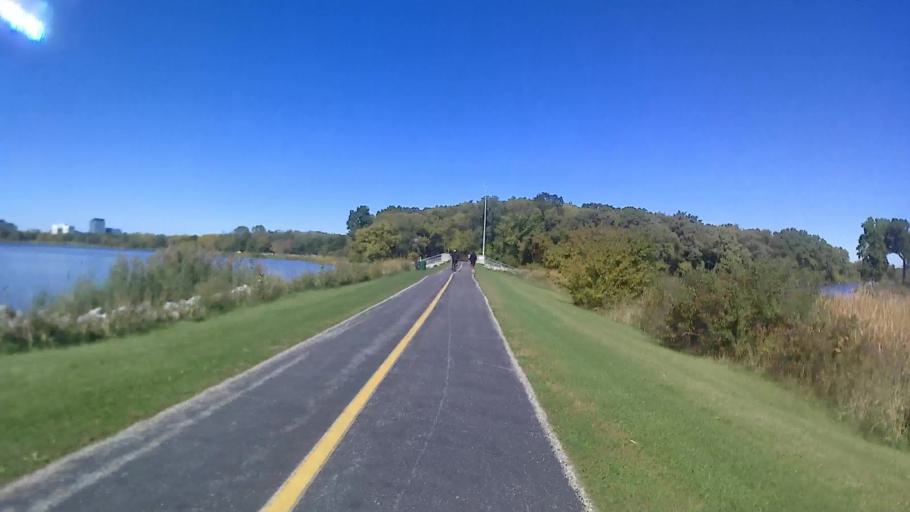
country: US
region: Illinois
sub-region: DuPage County
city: Itasca
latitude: 42.0204
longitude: -88.0149
